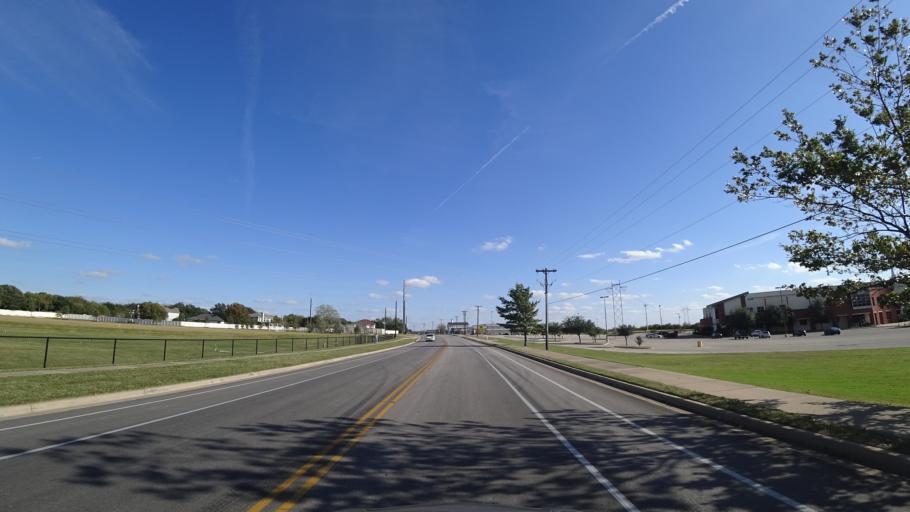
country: US
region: Texas
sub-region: Travis County
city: Wells Branch
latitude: 30.4595
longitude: -97.6916
